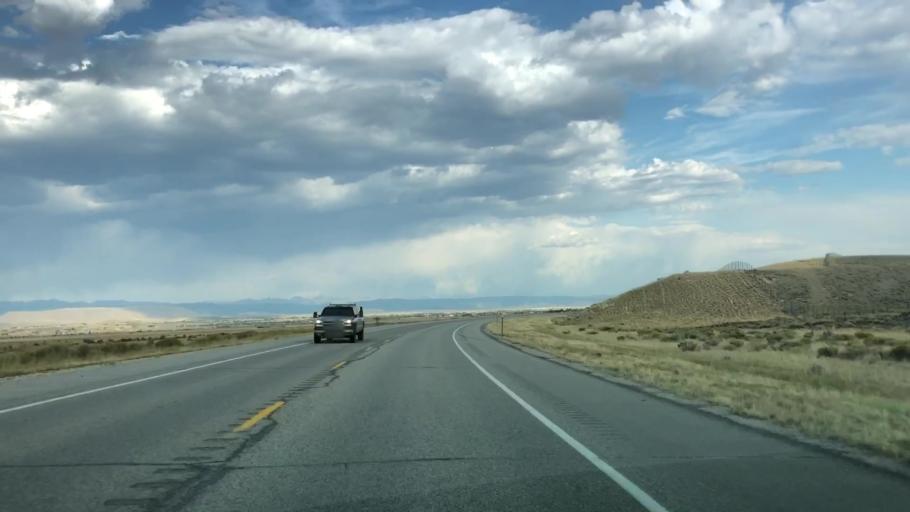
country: US
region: Wyoming
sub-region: Sublette County
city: Pinedale
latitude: 42.8747
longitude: -109.9424
